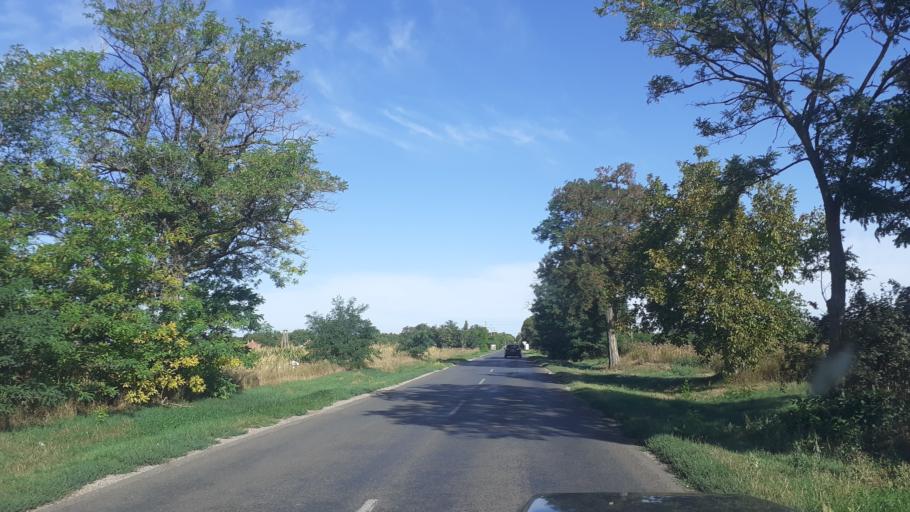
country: HU
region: Fejer
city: Ivancsa
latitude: 47.1832
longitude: 18.8027
